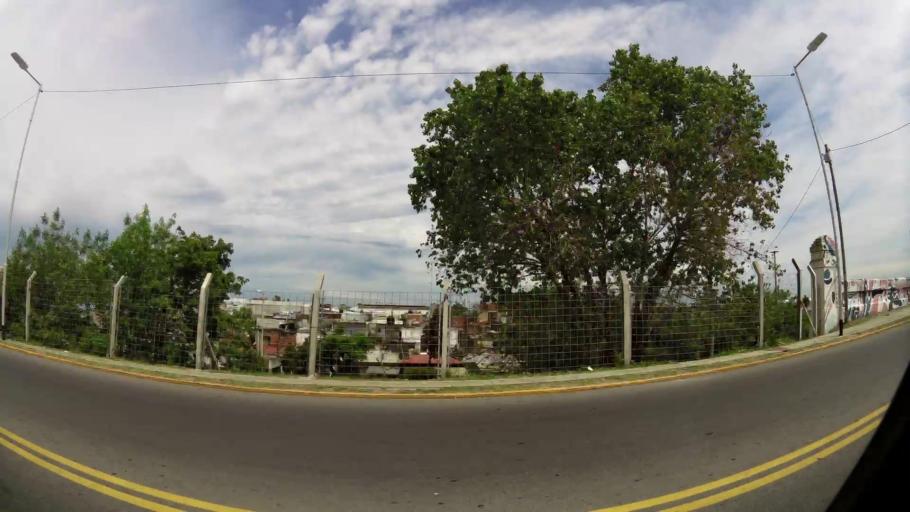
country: AR
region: Buenos Aires
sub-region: Partido de Avellaneda
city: Avellaneda
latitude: -34.6746
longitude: -58.3727
